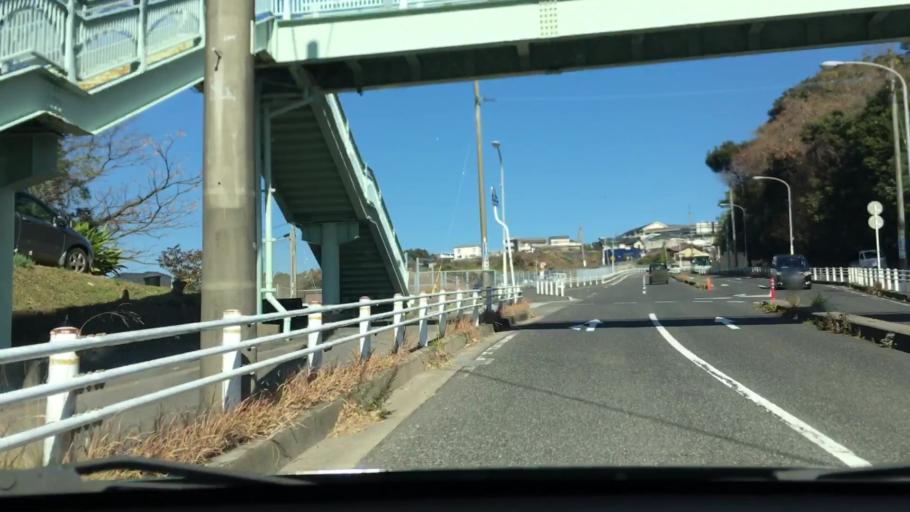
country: JP
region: Kagoshima
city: Kagoshima-shi
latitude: 31.5575
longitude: 130.5261
